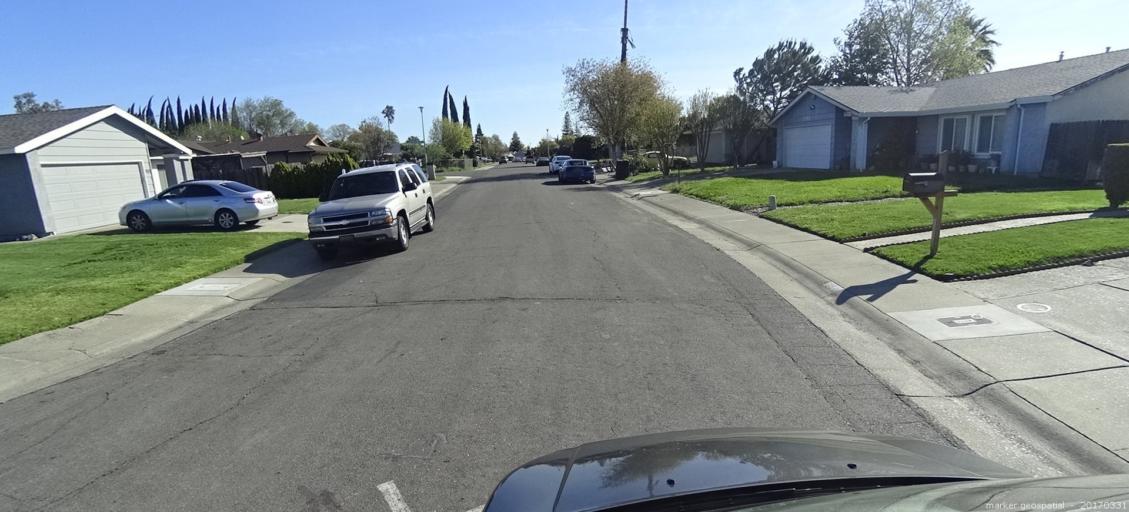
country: US
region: California
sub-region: Sacramento County
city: Parkway
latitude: 38.4678
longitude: -121.4613
